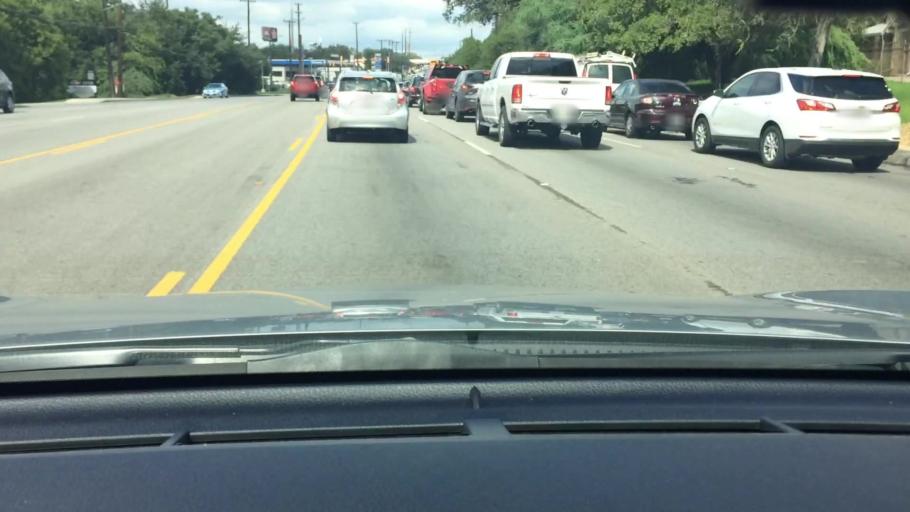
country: US
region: Texas
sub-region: Bexar County
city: Shavano Park
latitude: 29.5412
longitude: -98.5823
